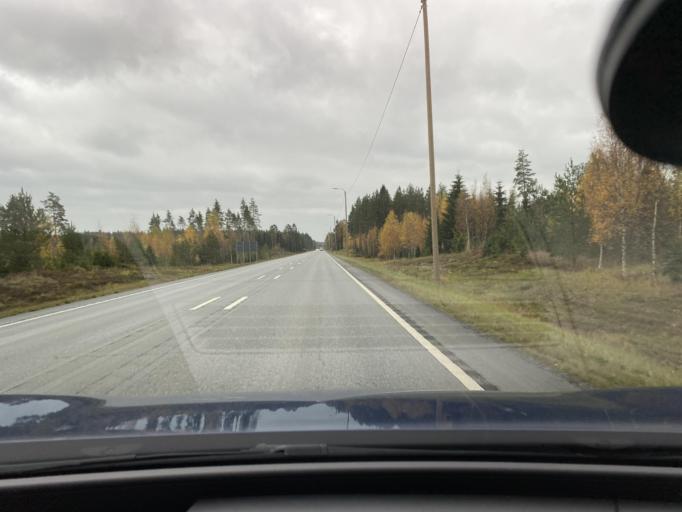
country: FI
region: Varsinais-Suomi
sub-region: Vakka-Suomi
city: Laitila
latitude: 60.9554
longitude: 21.5966
